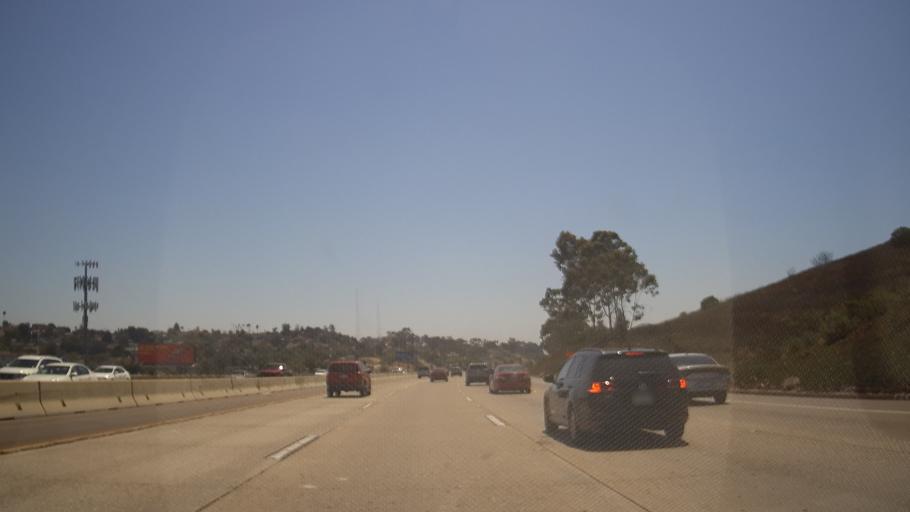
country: US
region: California
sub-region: San Diego County
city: Lemon Grove
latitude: 32.7343
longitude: -117.0594
